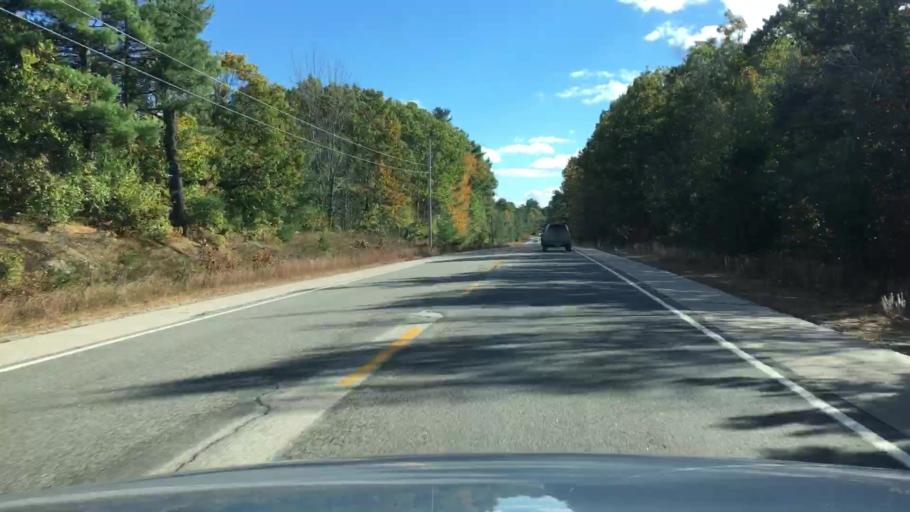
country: US
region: Maine
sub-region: York County
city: South Sanford
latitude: 43.3887
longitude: -70.6910
